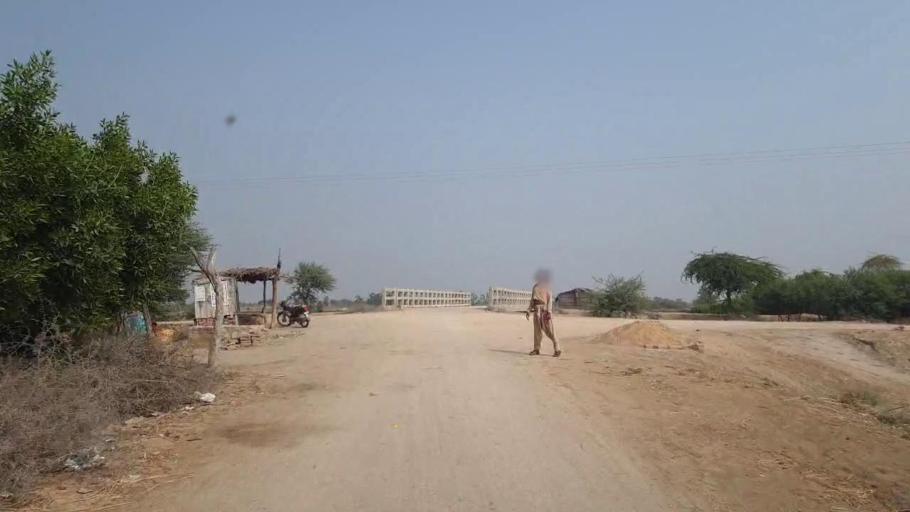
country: PK
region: Sindh
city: Kario
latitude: 24.9127
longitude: 68.6025
